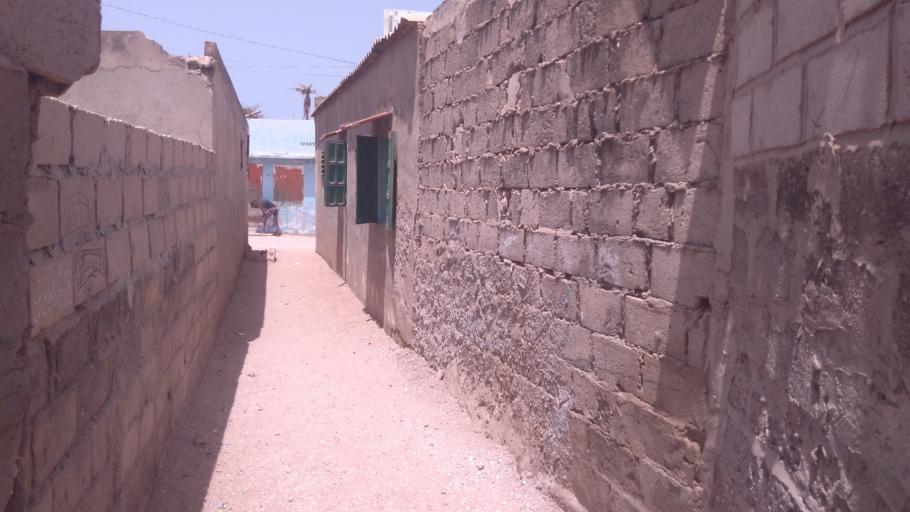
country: SN
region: Dakar
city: Pikine
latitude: 14.6871
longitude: -17.2276
